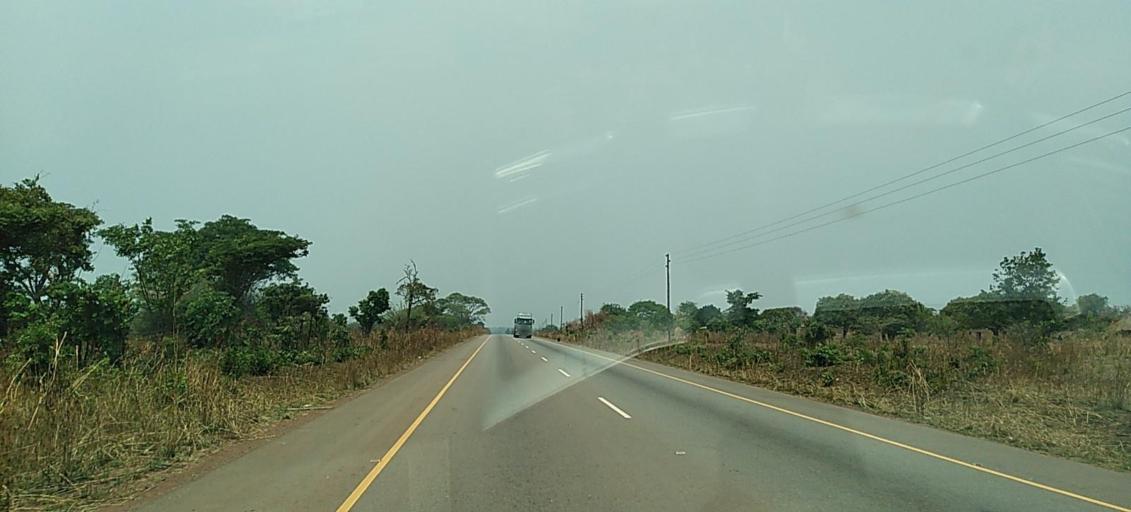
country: ZM
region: Copperbelt
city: Chililabombwe
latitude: -12.5169
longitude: 27.5652
